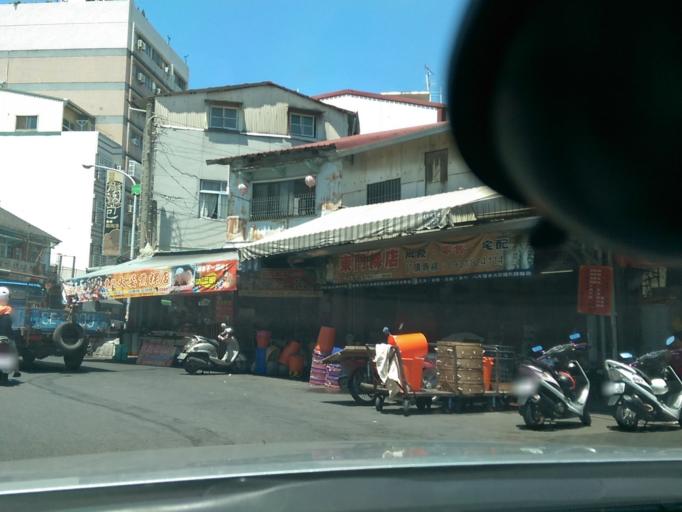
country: TW
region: Taiwan
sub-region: Chiayi
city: Jiayi Shi
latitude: 23.4805
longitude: 120.4568
